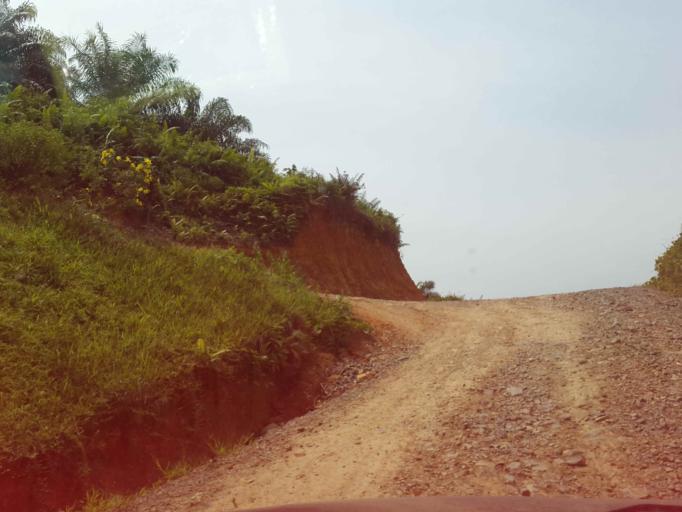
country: MY
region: Sarawak
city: Kuching
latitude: 0.9436
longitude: 110.2922
